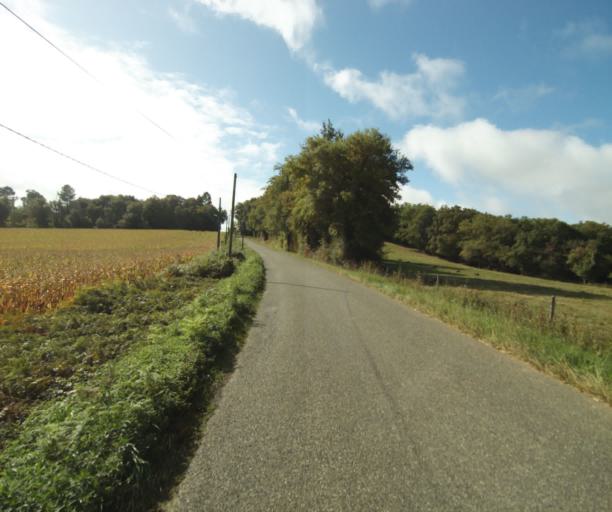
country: FR
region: Midi-Pyrenees
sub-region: Departement du Gers
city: Cazaubon
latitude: 43.8461
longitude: -0.0561
